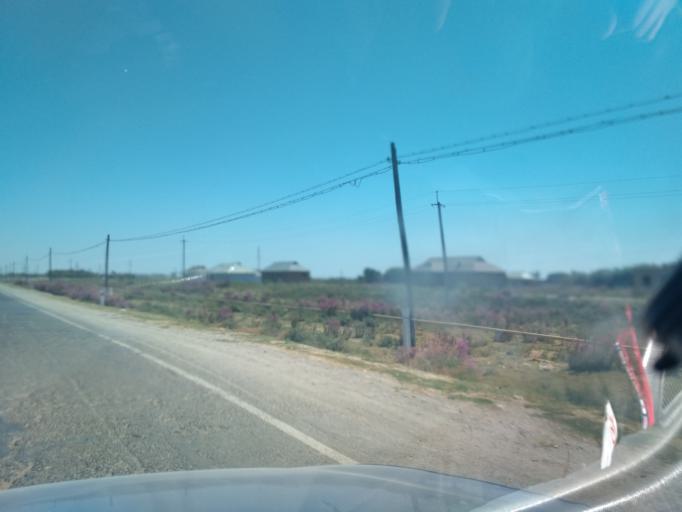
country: UZ
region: Sirdaryo
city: Guliston
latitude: 40.4907
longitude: 68.7122
